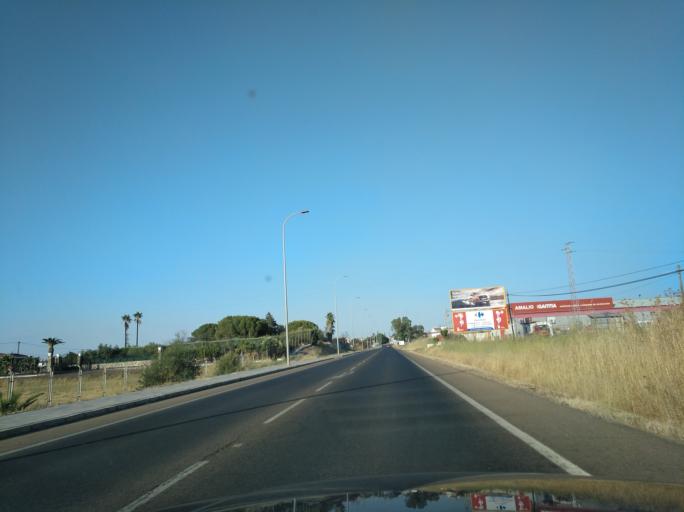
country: ES
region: Extremadura
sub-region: Provincia de Badajoz
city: Badajoz
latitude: 38.8562
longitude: -6.9955
